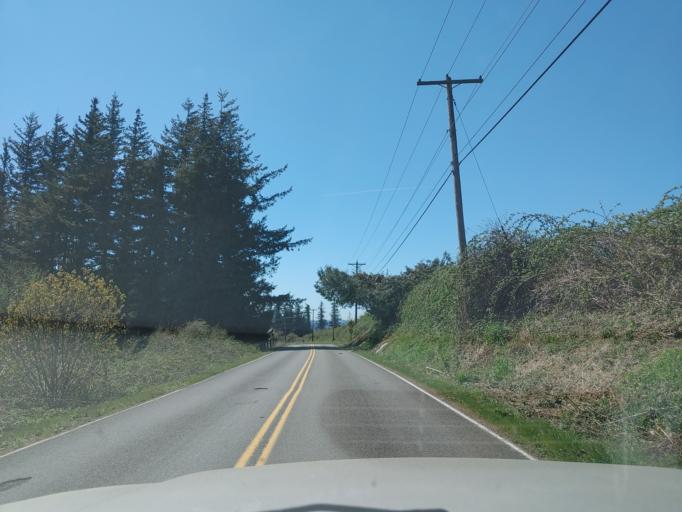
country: US
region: Washington
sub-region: Clark County
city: Washougal
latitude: 45.5262
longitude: -122.3127
